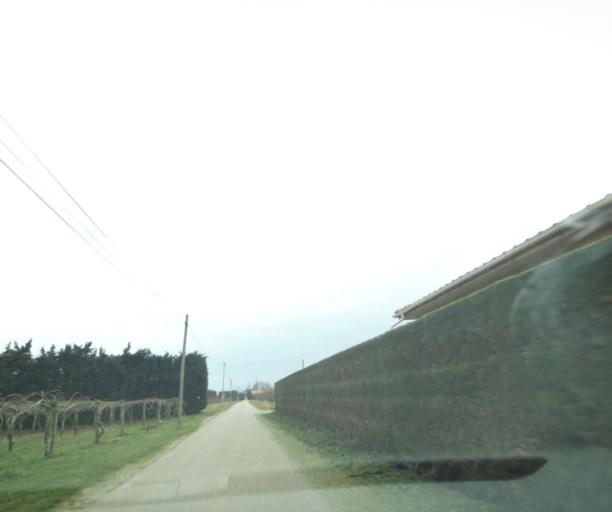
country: FR
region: Rhone-Alpes
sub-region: Departement de la Drome
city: Chateauneuf-sur-Isere
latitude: 44.9880
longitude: 4.9319
